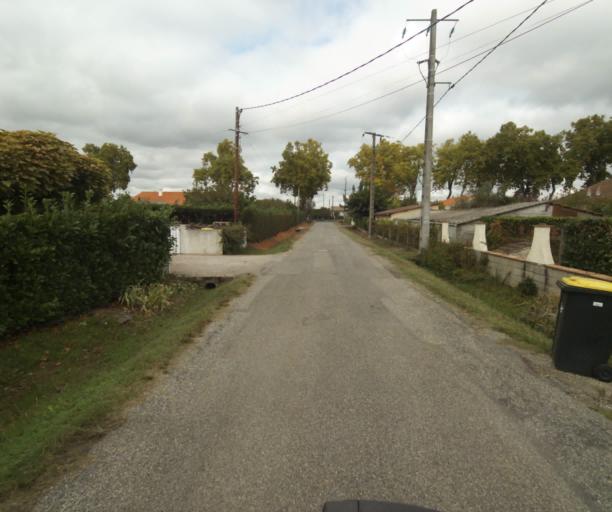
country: FR
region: Midi-Pyrenees
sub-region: Departement du Tarn-et-Garonne
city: Montech
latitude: 43.9637
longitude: 1.2532
